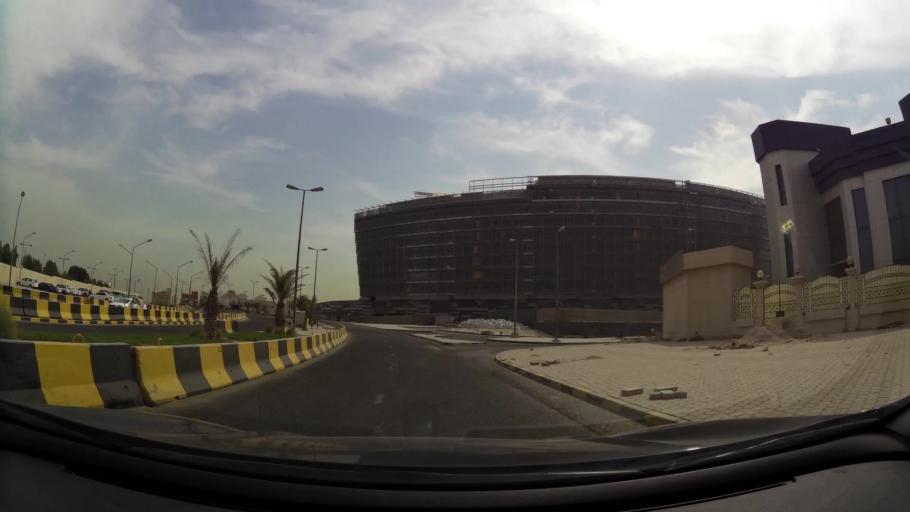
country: KW
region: Al Farwaniyah
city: Janub as Surrah
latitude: 29.2740
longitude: 48.0191
